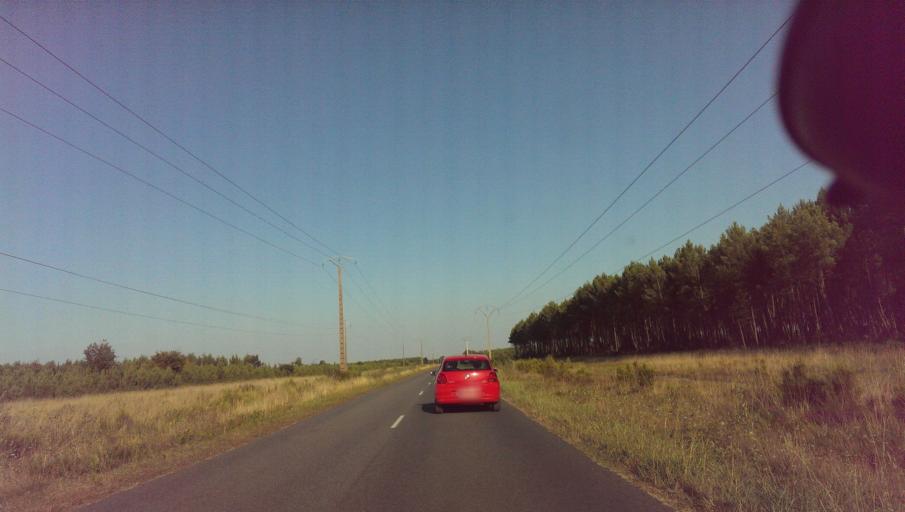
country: FR
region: Aquitaine
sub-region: Departement des Landes
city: Mimizan
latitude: 44.1852
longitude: -1.1950
